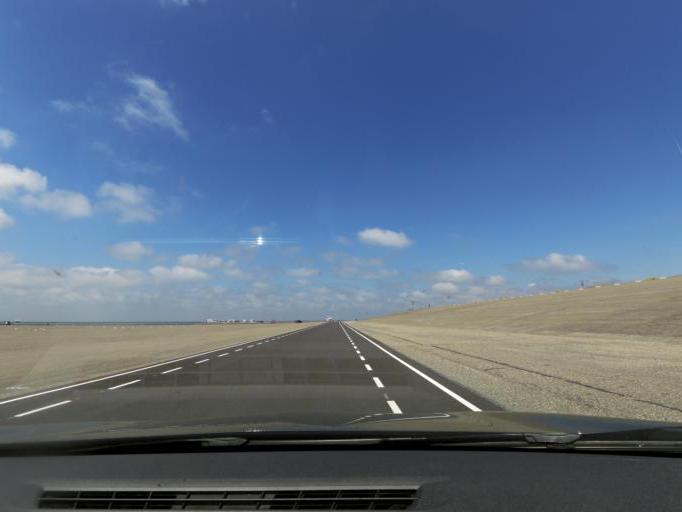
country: NL
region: Zeeland
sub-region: Schouwen-Duiveland
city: Scharendijke
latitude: 51.7465
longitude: 3.8247
